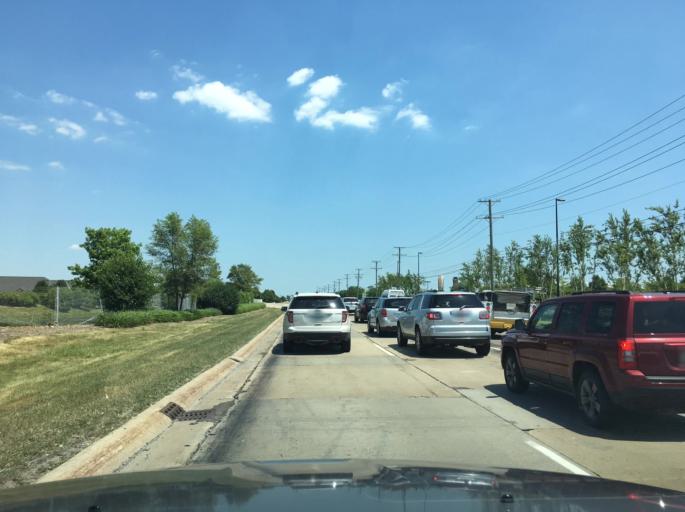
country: US
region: Michigan
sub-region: Macomb County
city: Clinton
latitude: 42.6277
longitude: -82.9464
